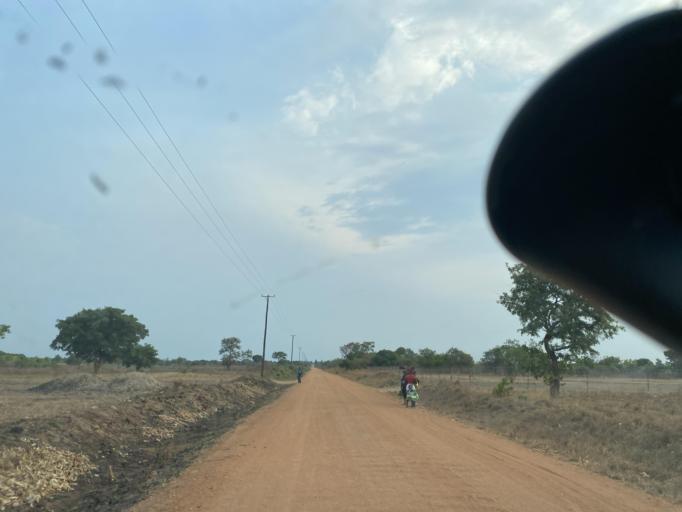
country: ZM
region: Lusaka
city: Chongwe
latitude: -15.2045
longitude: 28.5809
